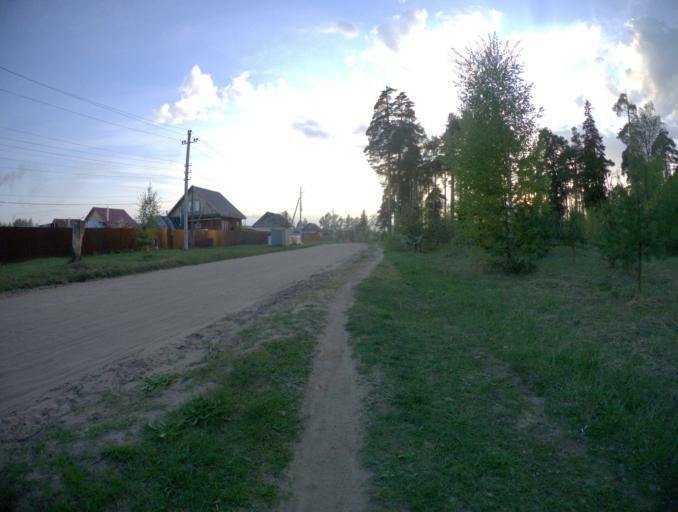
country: RU
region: Ivanovo
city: Yuzha
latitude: 56.5749
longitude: 42.0197
